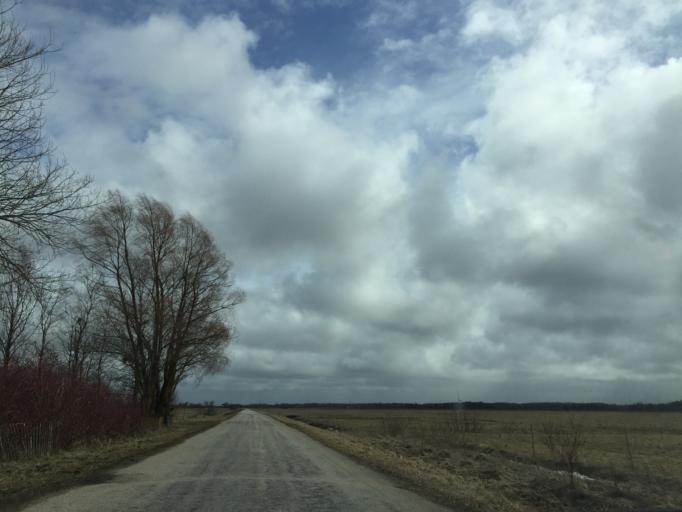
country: EE
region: Laeaene
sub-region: Lihula vald
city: Lihula
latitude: 58.7316
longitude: 23.8743
